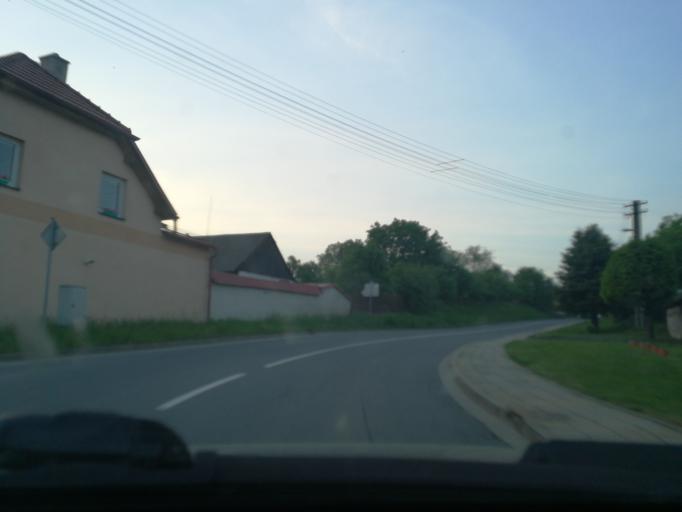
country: CZ
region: Zlin
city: Tlumacov
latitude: 49.2772
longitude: 17.5482
